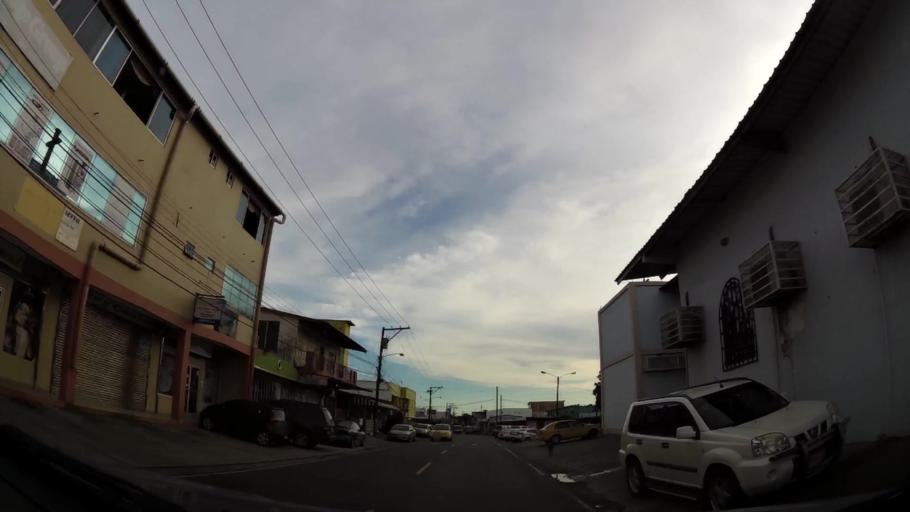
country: PA
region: Panama
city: La Chorrera
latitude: 8.8831
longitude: -79.7798
